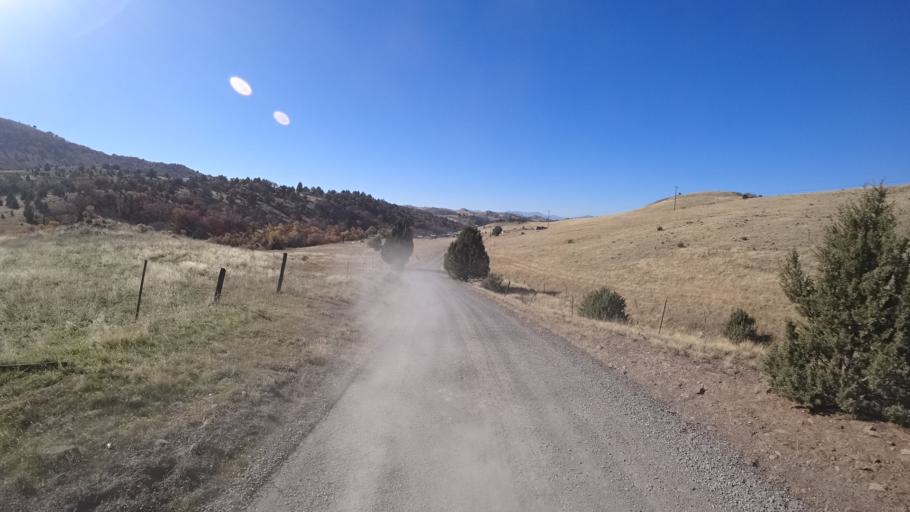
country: US
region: California
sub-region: Siskiyou County
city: Montague
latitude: 41.7949
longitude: -122.3378
